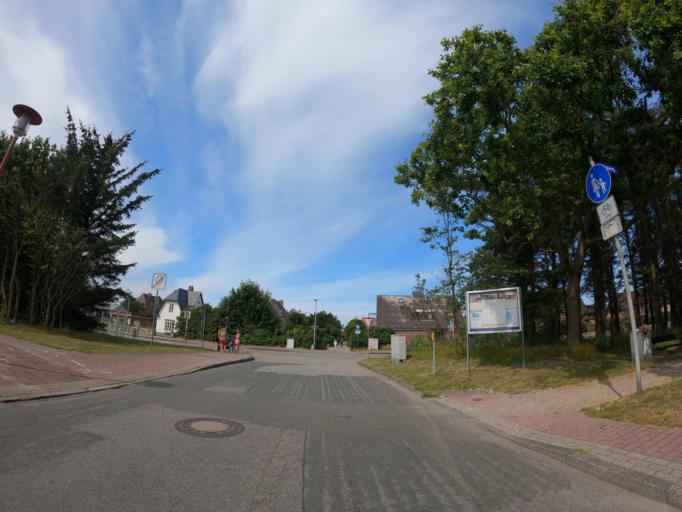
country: DE
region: Schleswig-Holstein
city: Westerland
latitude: 54.9208
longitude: 8.3104
